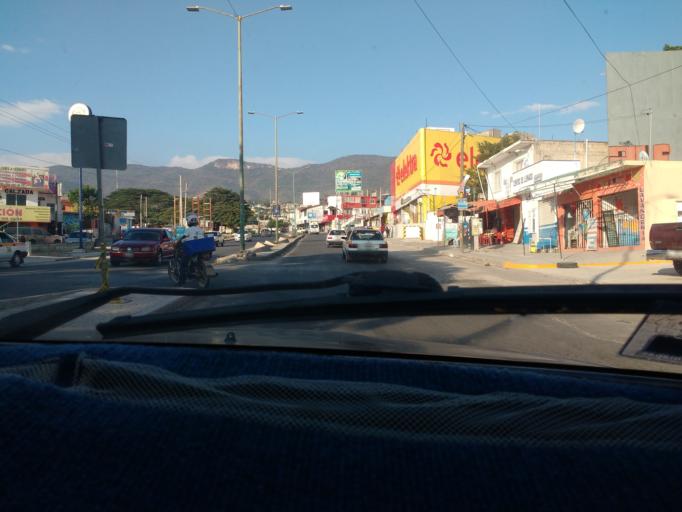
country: MX
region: Chiapas
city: Tuxtla Gutierrez
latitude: 16.7759
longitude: -93.1016
